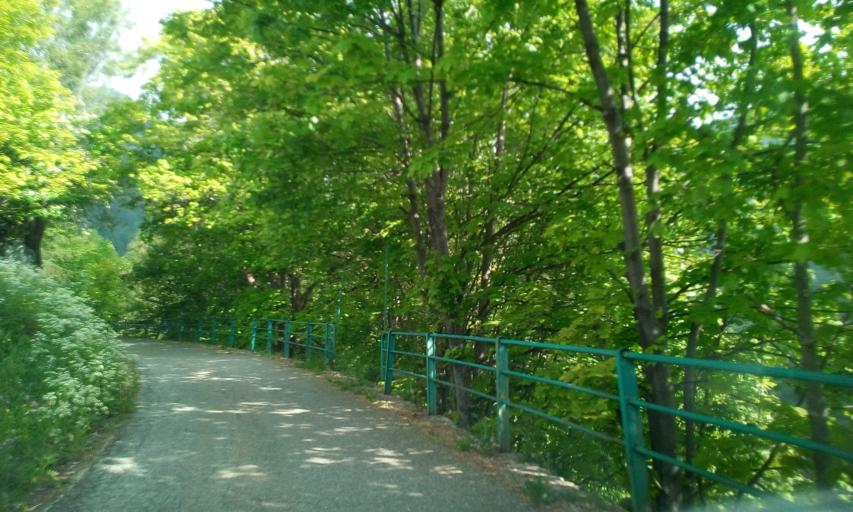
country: IT
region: Aosta Valley
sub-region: Valle d'Aosta
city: Antey-Saint-Andre
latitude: 45.8185
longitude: 7.5789
